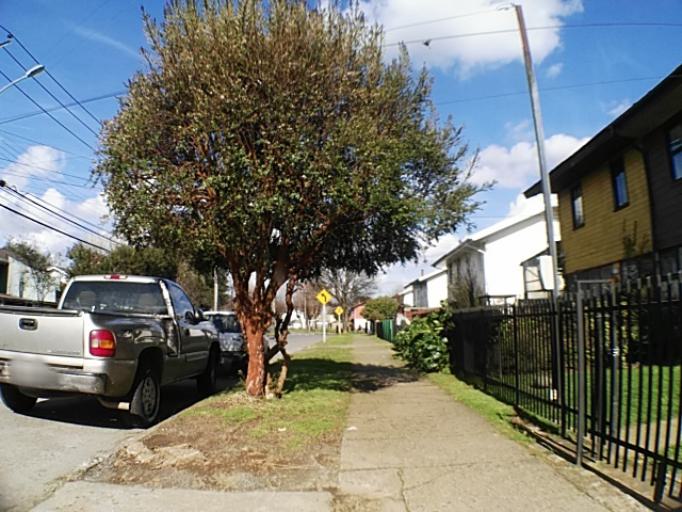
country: CL
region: Los Rios
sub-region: Provincia de Valdivia
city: Valdivia
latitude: -39.8350
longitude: -73.2398
